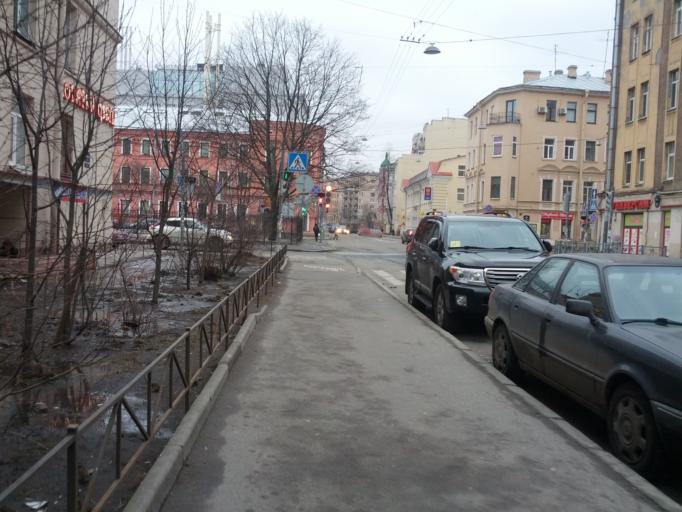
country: RU
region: St.-Petersburg
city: Petrogradka
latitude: 59.9585
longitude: 30.3127
